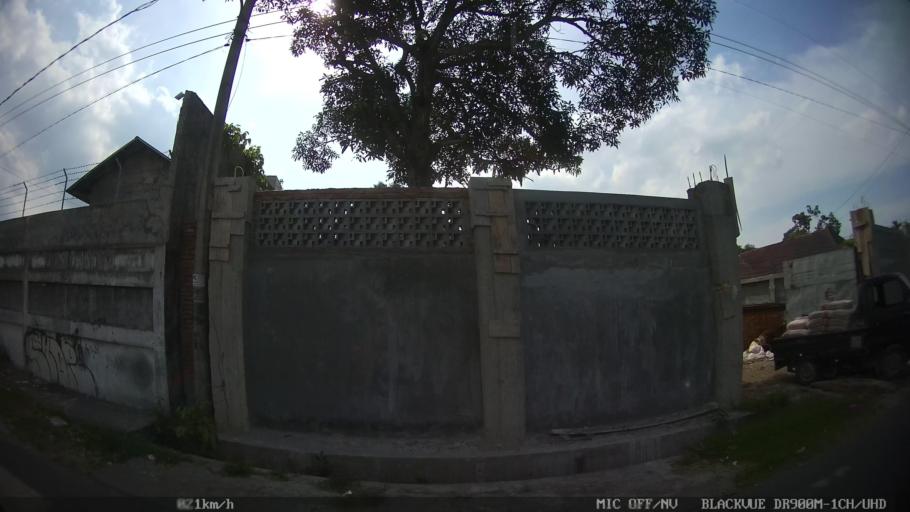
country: ID
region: North Sumatra
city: Binjai
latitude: 3.6119
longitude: 98.4983
